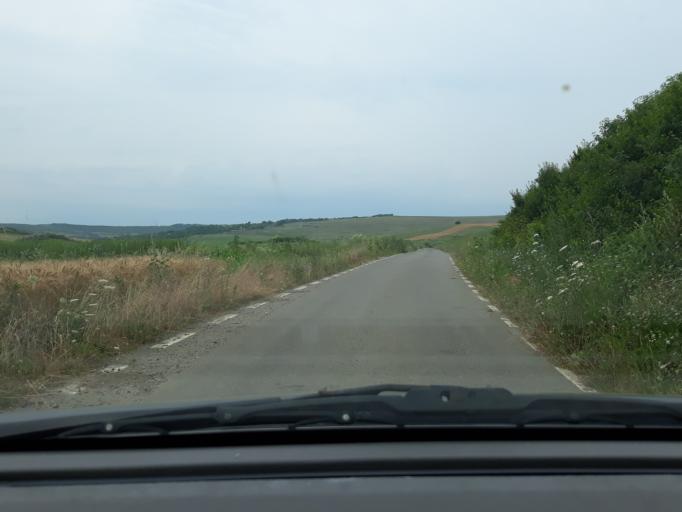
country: RO
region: Salaj
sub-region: Comuna Criseni
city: Criseni
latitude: 47.2750
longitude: 23.0781
